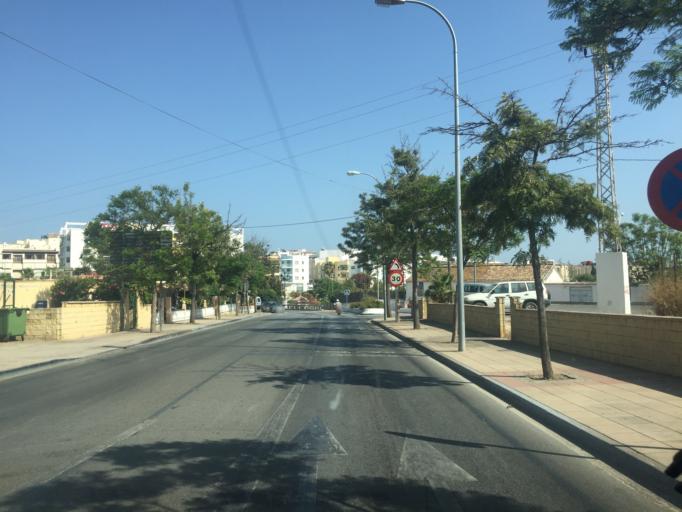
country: ES
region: Andalusia
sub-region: Provincia de Malaga
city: Nerja
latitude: 36.7487
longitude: -3.8826
